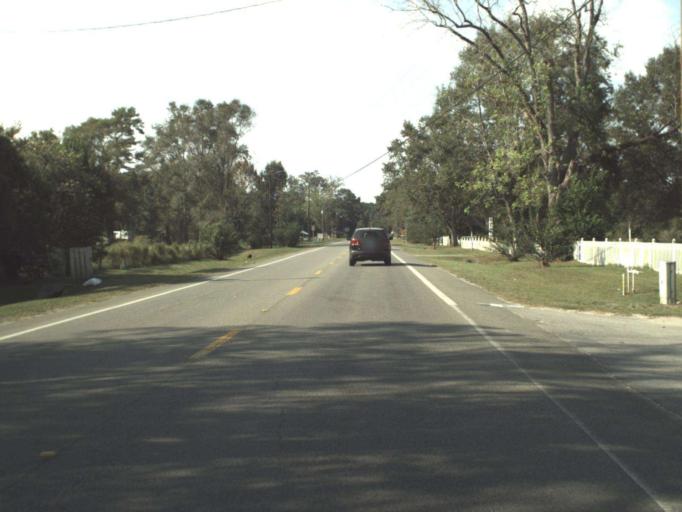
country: US
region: Florida
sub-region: Gulf County
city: Wewahitchka
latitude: 30.0960
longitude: -85.1978
